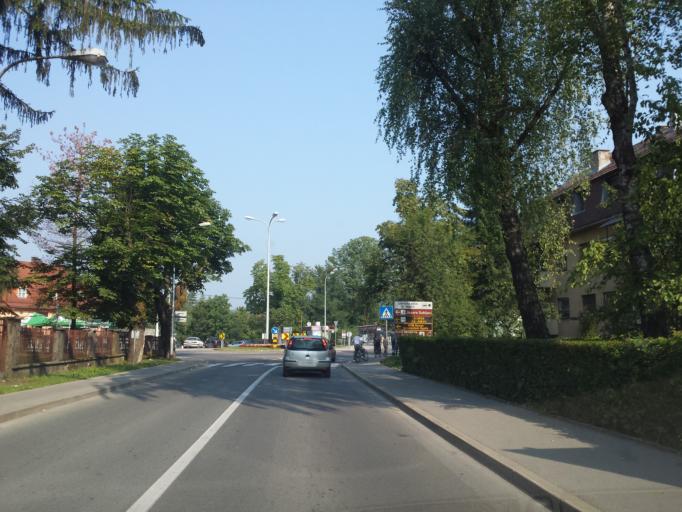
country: HR
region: Karlovacka
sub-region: Grad Ogulin
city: Ogulin
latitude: 45.2623
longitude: 15.2271
